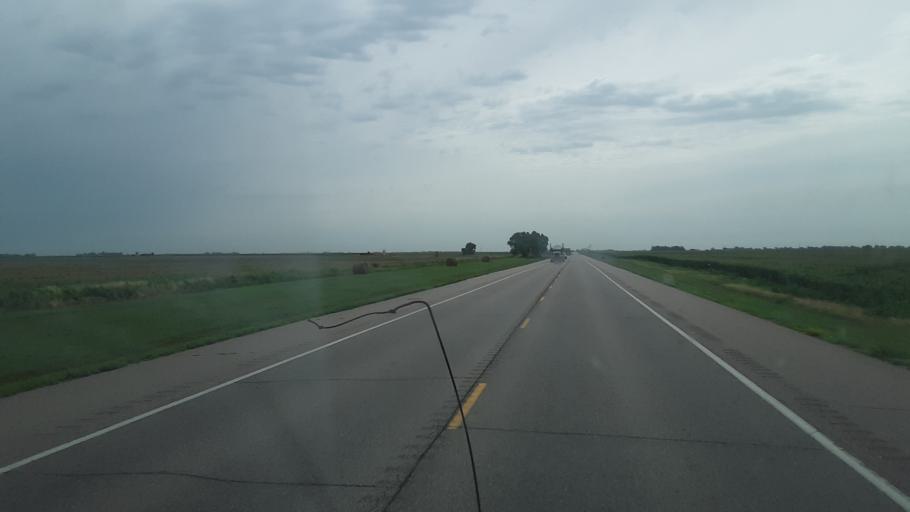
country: US
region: Kansas
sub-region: Stafford County
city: Saint John
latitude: 37.9561
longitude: -98.8868
